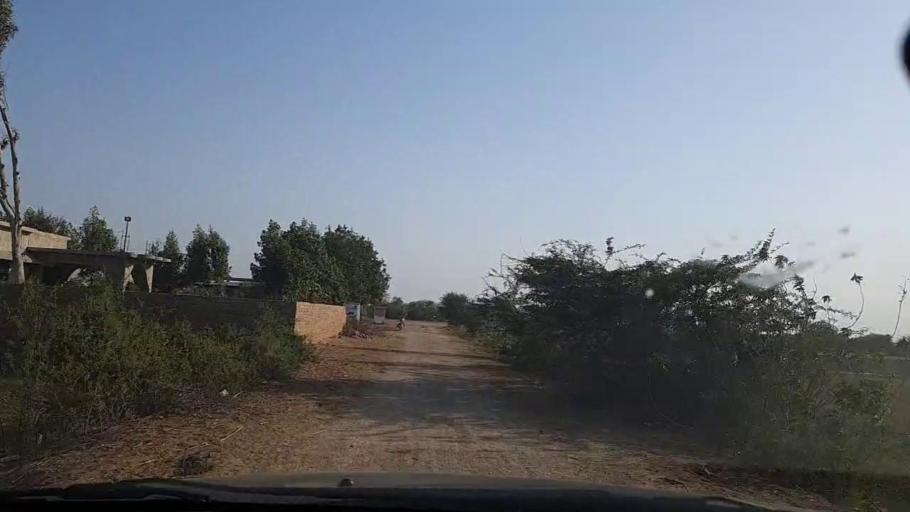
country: PK
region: Sindh
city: Chuhar Jamali
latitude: 24.5515
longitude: 68.1070
